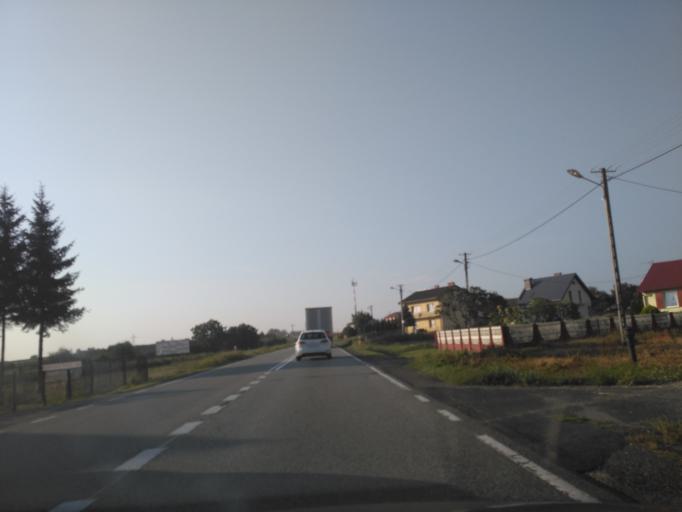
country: PL
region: Lublin Voivodeship
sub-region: Powiat krasnicki
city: Szastarka
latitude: 50.8224
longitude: 22.3149
